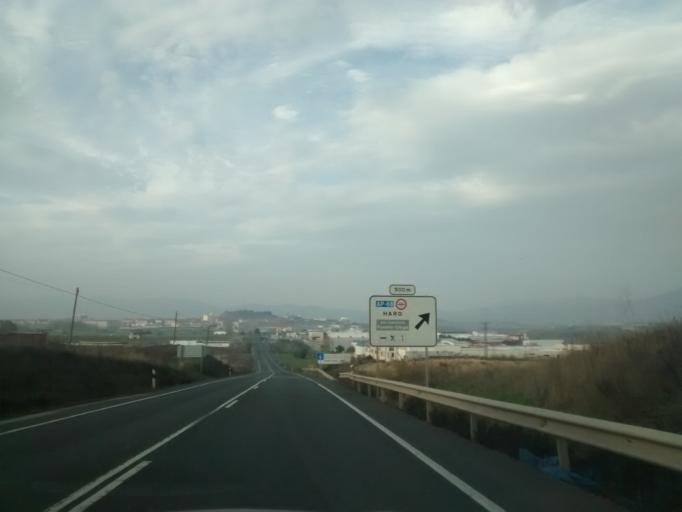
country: ES
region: La Rioja
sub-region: Provincia de La Rioja
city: Ollauri
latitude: 42.5555
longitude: -2.8353
